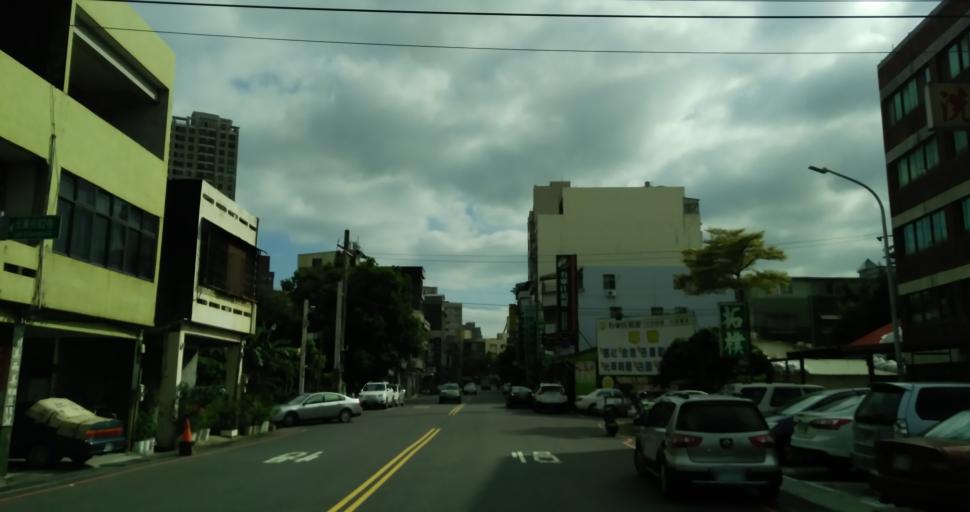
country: TW
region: Taiwan
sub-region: Hsinchu
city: Hsinchu
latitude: 24.8161
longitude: 120.9723
